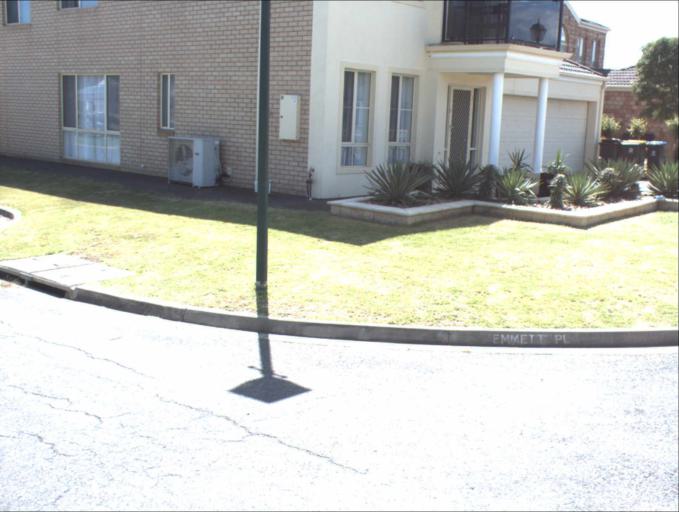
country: AU
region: South Australia
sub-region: Port Adelaide Enfield
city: Gilles Plains
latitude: -34.8507
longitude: 138.6483
